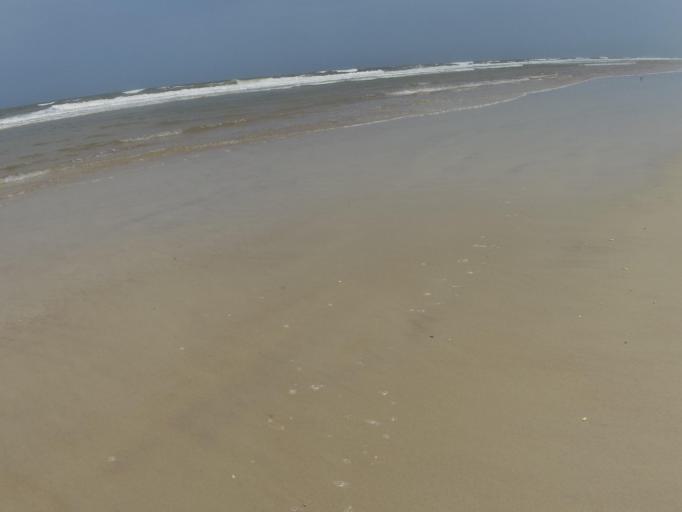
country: US
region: Florida
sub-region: Saint Johns County
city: Saint Augustine
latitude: 29.8976
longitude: -81.2763
